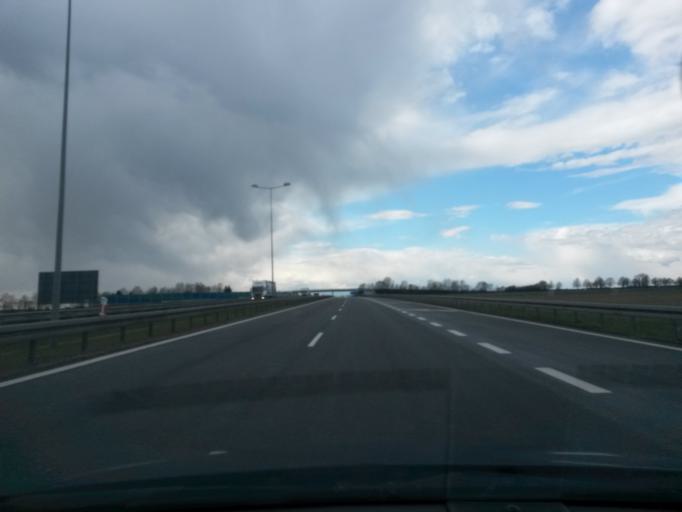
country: PL
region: Greater Poland Voivodeship
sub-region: Powiat koninski
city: Rzgow Pierwszy
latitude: 52.2063
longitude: 18.0167
